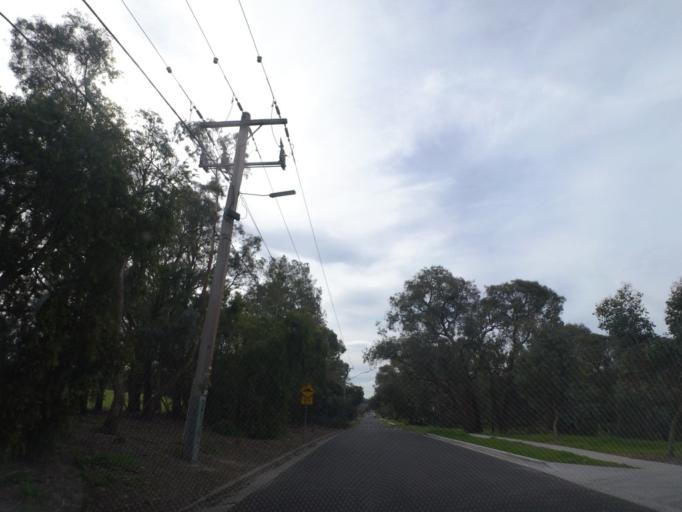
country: AU
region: Victoria
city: Mitcham
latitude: -37.8240
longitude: 145.2019
